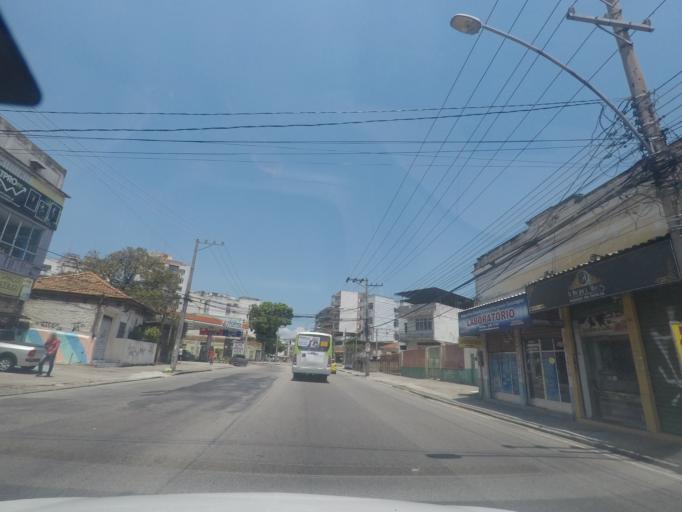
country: BR
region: Rio de Janeiro
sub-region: Duque De Caxias
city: Duque de Caxias
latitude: -22.8407
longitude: -43.3051
